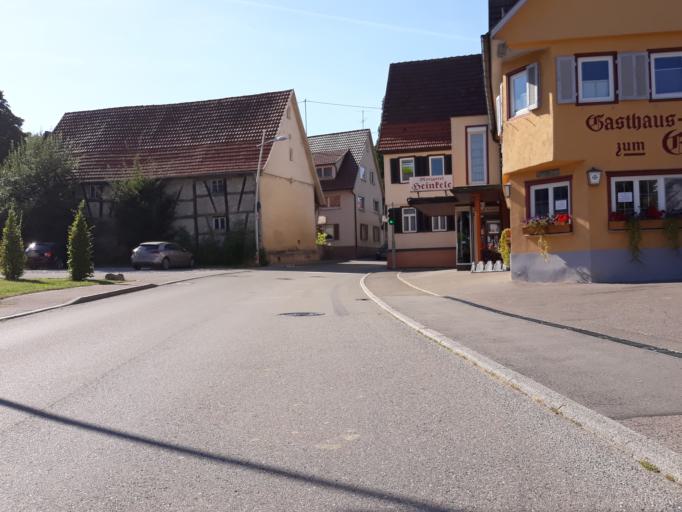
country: DE
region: Baden-Wuerttemberg
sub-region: Regierungsbezirk Stuttgart
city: Weil der Stadt
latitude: 48.7165
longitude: 8.8874
